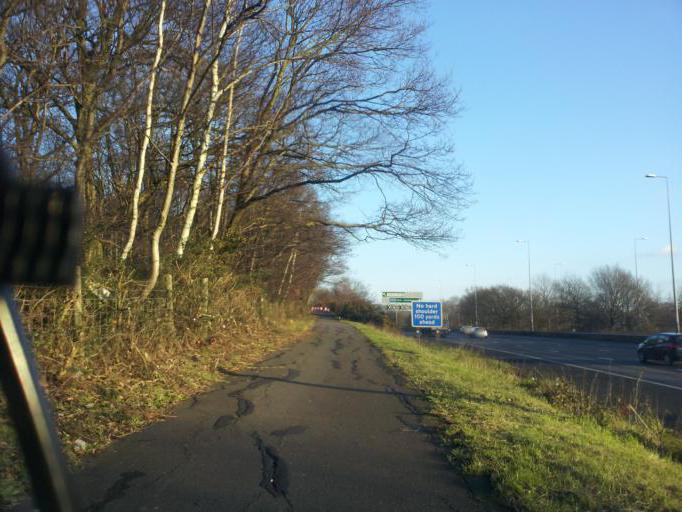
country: GB
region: England
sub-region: Medway
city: Cuxton
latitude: 51.4016
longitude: 0.4129
